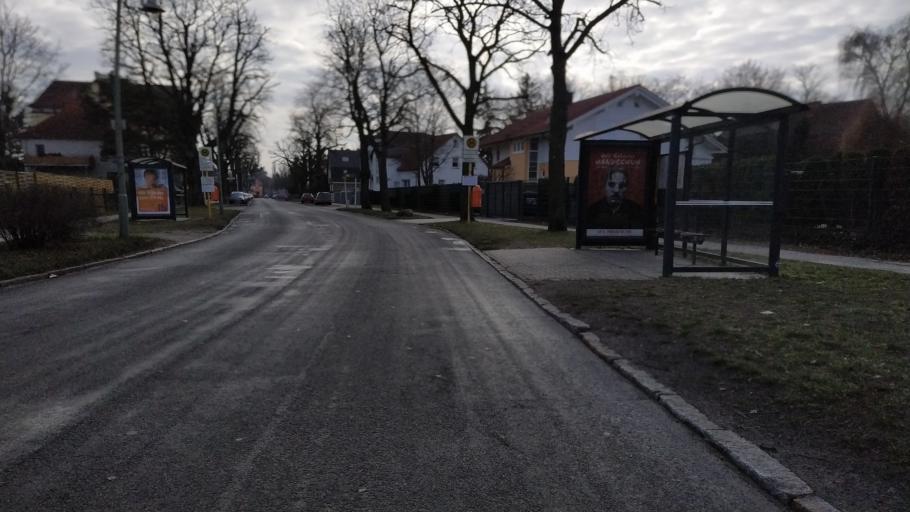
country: DE
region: Berlin
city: Mahlsdorf
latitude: 52.5165
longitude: 13.6089
